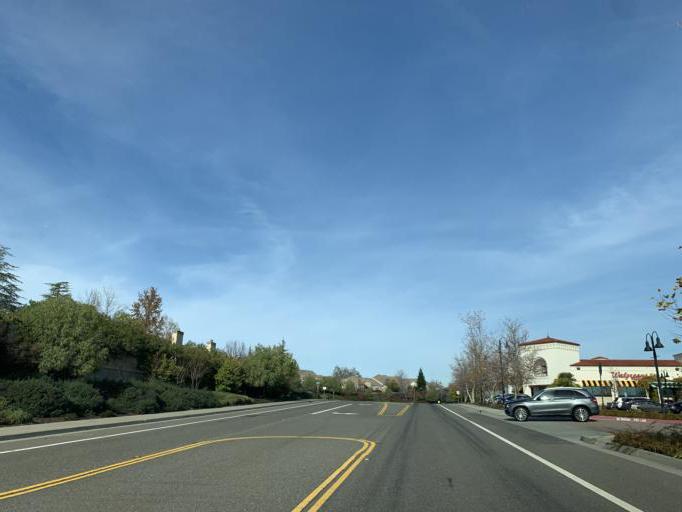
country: US
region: California
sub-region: El Dorado County
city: El Dorado Hills
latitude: 38.6550
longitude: -121.0724
